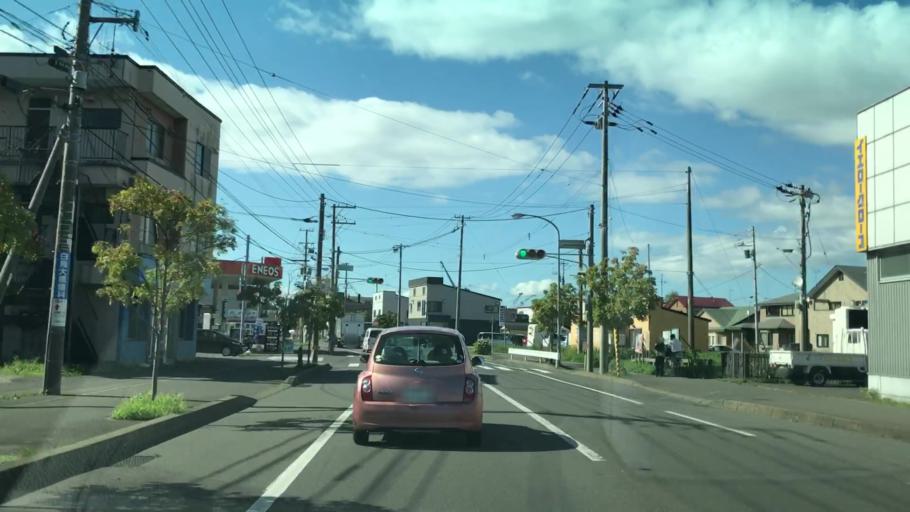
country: JP
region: Hokkaido
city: Muroran
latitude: 42.3333
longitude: 140.9625
